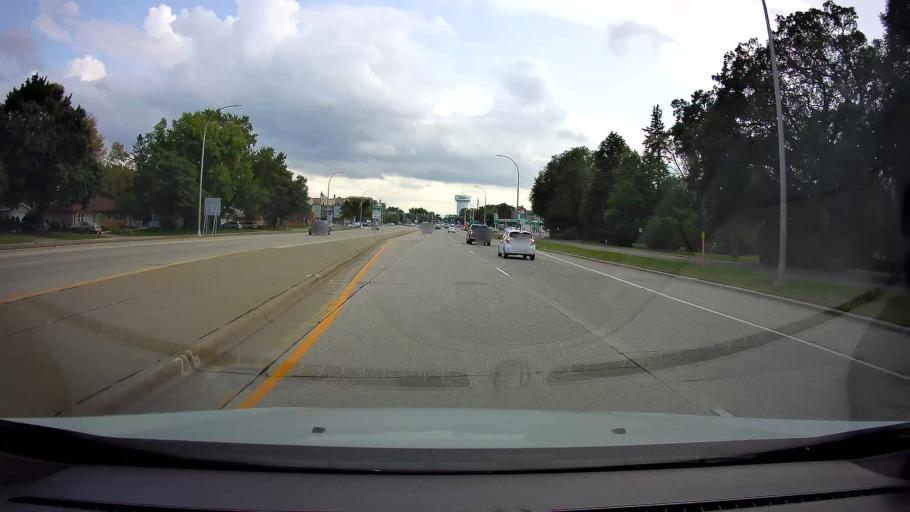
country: US
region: Minnesota
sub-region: Ramsey County
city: Falcon Heights
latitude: 44.9943
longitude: -93.1667
